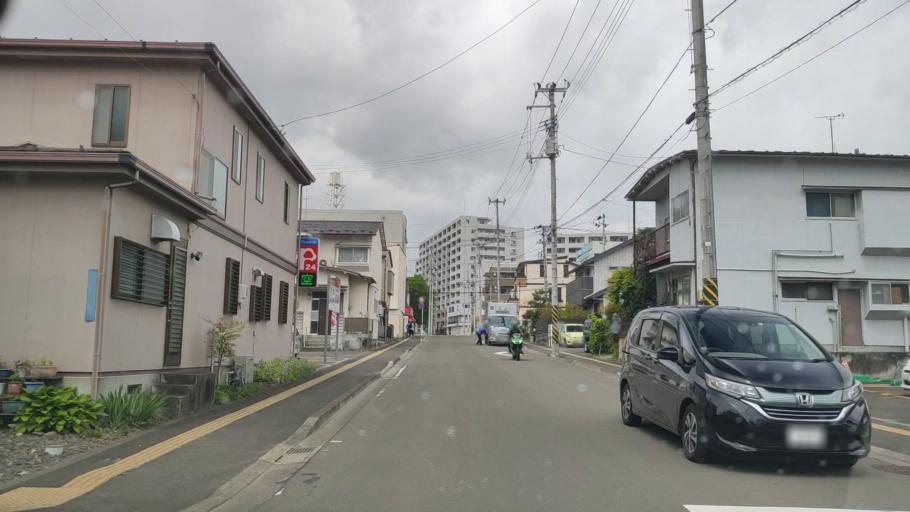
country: JP
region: Miyagi
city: Sendai-shi
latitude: 38.2555
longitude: 140.8978
